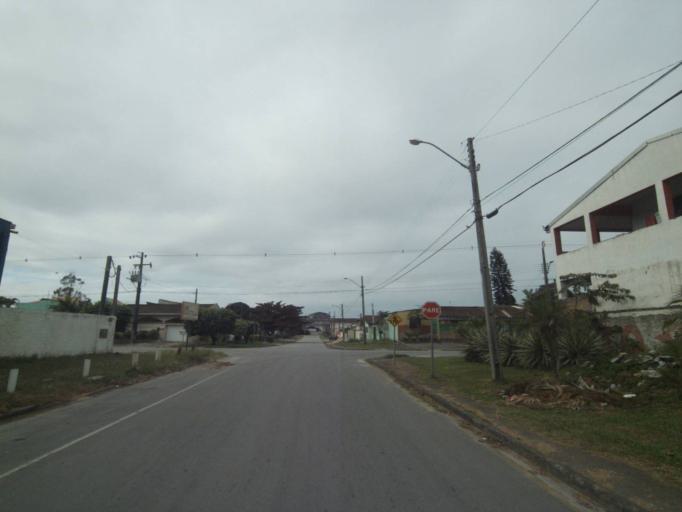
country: BR
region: Parana
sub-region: Paranagua
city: Paranagua
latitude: -25.5183
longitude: -48.5301
